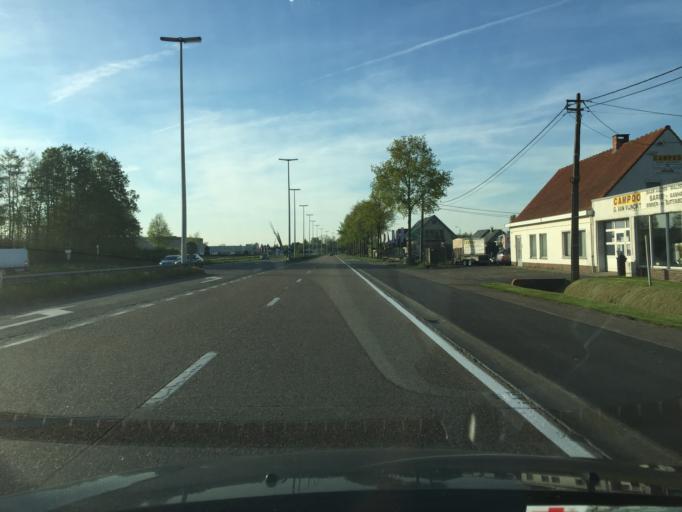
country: BE
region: Flanders
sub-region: Provincie Oost-Vlaanderen
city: Knesselare
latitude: 51.1215
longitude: 3.4271
